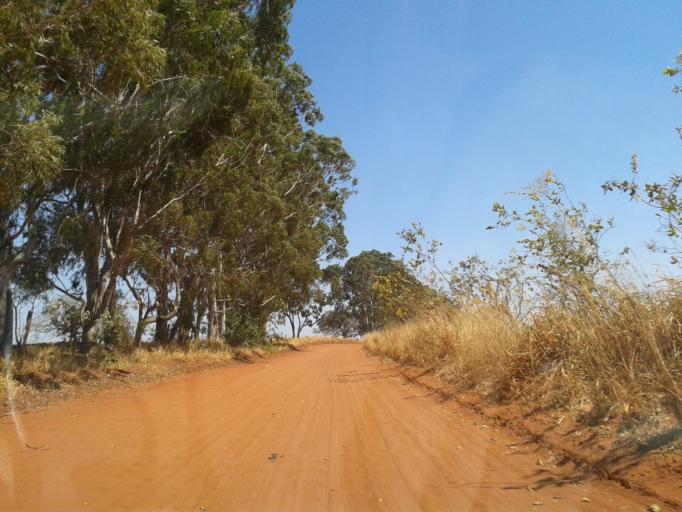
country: BR
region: Minas Gerais
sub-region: Ituiutaba
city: Ituiutaba
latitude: -18.9935
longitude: -49.3791
